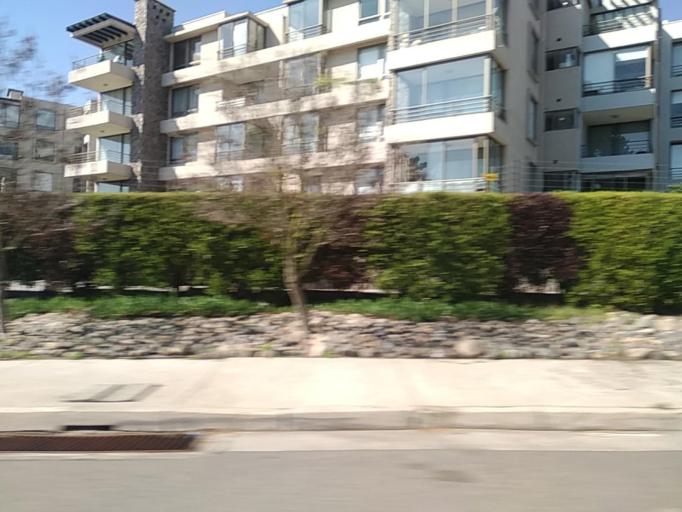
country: CL
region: Valparaiso
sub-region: Provincia de Valparaiso
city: Vina del Mar
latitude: -32.9416
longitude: -71.5371
